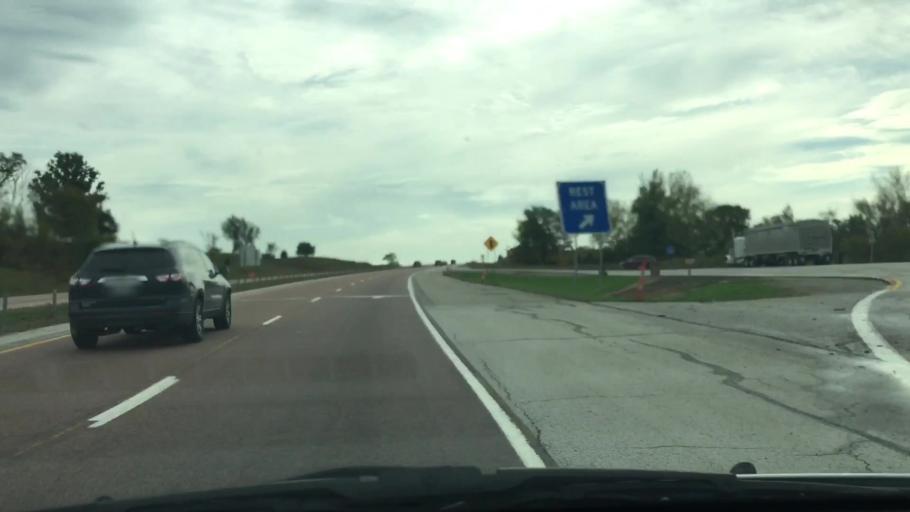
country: US
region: Iowa
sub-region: Warren County
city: Norwalk
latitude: 41.2793
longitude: -93.7789
